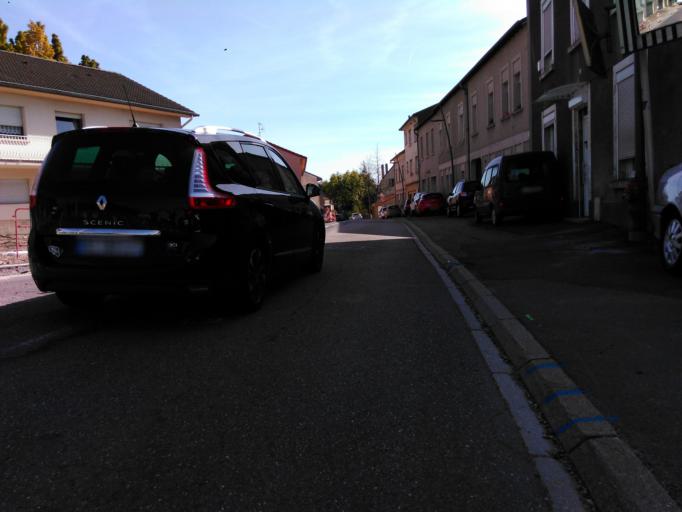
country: FR
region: Lorraine
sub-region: Departement de la Moselle
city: Hettange-Grande
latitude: 49.4069
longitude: 6.1498
